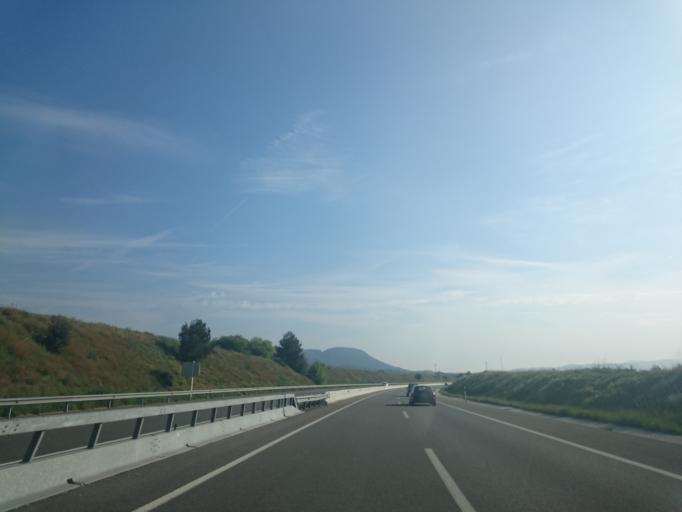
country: ES
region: Catalonia
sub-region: Provincia de Barcelona
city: Artes
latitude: 41.7931
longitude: 1.9175
